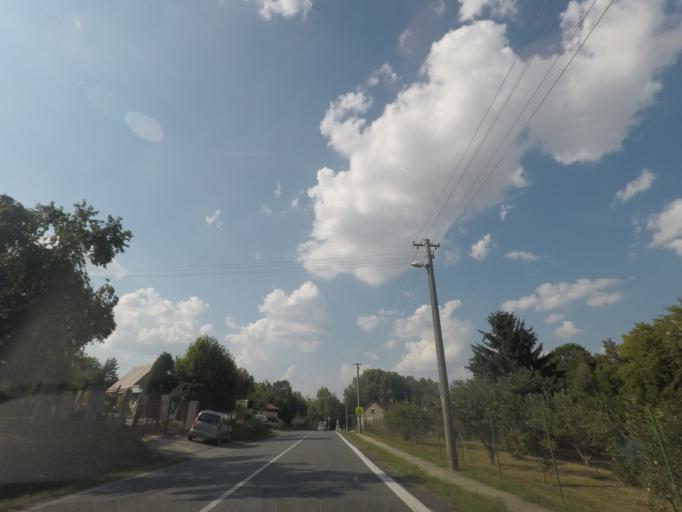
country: CZ
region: Kralovehradecky
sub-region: Okres Nachod
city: Jaromer
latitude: 50.3641
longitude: 15.9063
